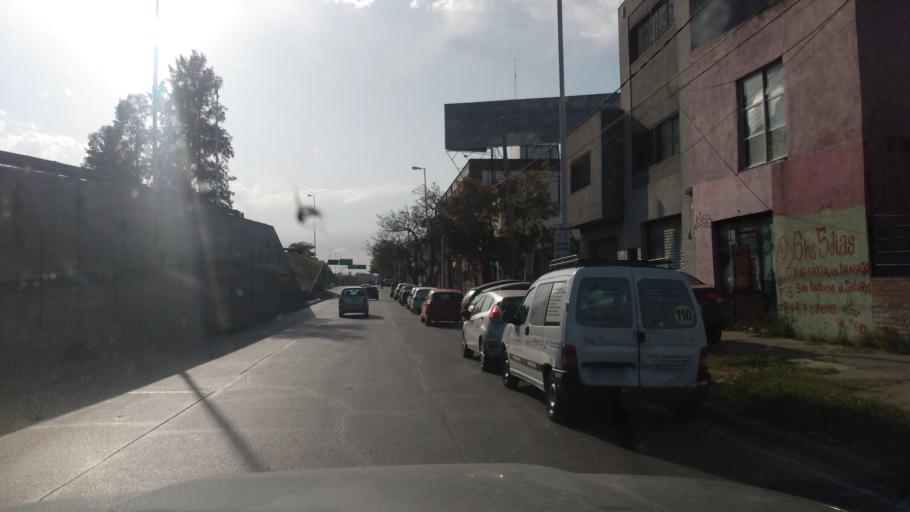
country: AR
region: Buenos Aires
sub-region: Partido de Moron
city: Moron
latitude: -34.6333
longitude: -58.6208
